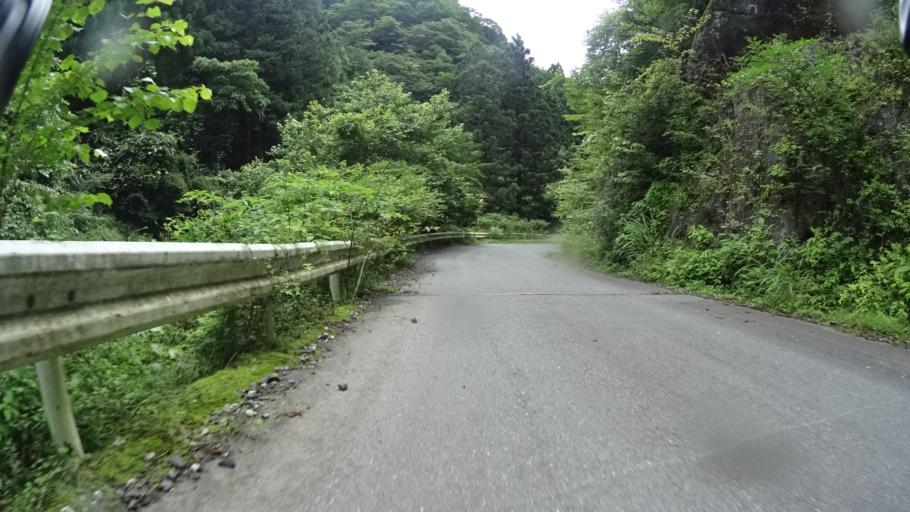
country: JP
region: Saitama
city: Chichibu
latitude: 35.8847
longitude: 139.1407
